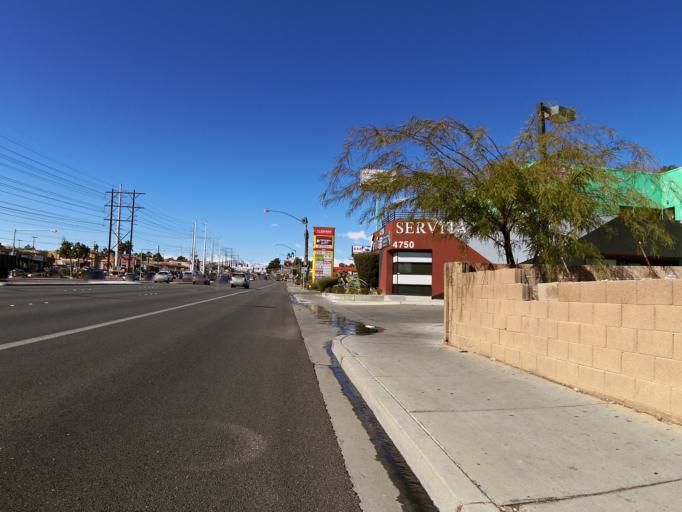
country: US
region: Nevada
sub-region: Clark County
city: Spring Valley
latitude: 36.1156
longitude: -115.2055
